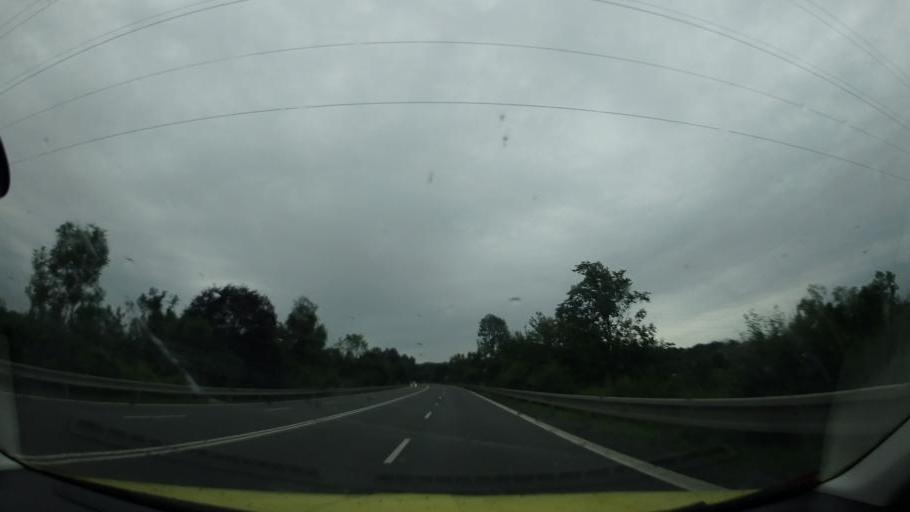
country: CZ
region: Olomoucky
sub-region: Okres Prerov
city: Hranice
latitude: 49.5657
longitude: 17.7658
